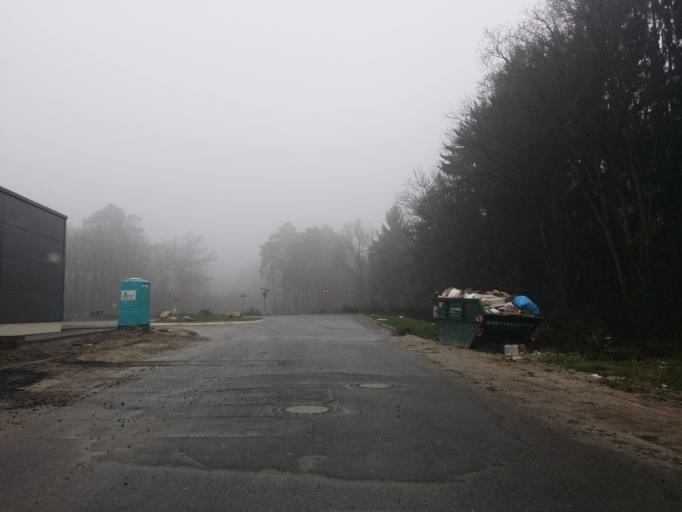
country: DE
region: Hesse
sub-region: Regierungsbezirk Darmstadt
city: Niedernhausen
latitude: 50.1417
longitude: 8.3323
